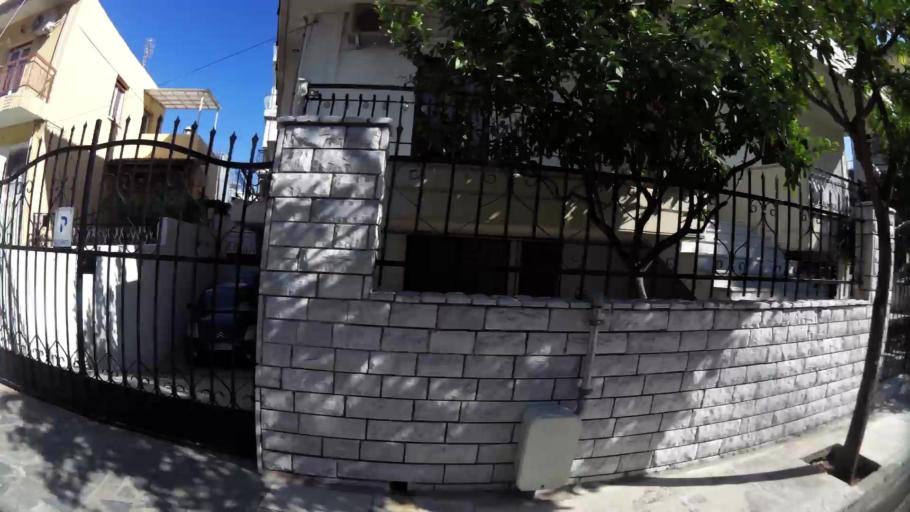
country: GR
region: Attica
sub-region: Nomarchia Athinas
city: Metamorfosi
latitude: 38.0657
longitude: 23.7569
